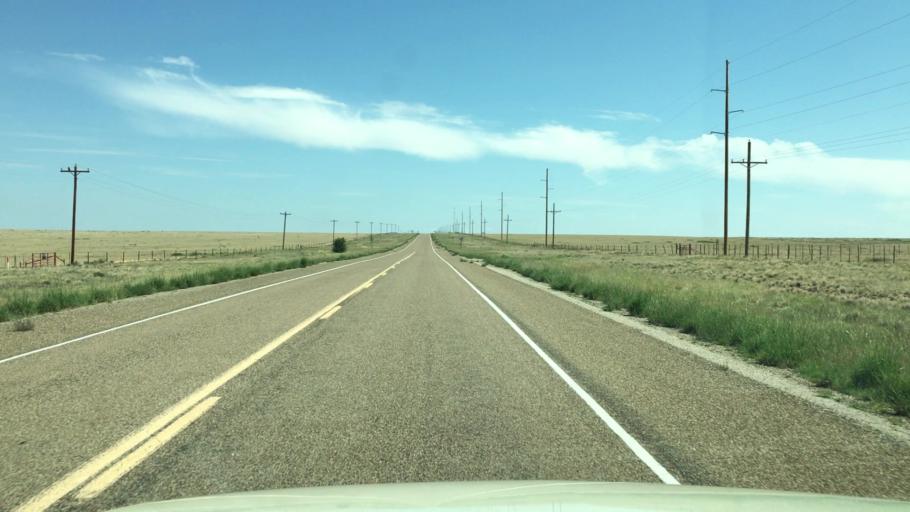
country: US
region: New Mexico
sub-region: Chaves County
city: Roswell
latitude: 33.9388
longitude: -104.5935
